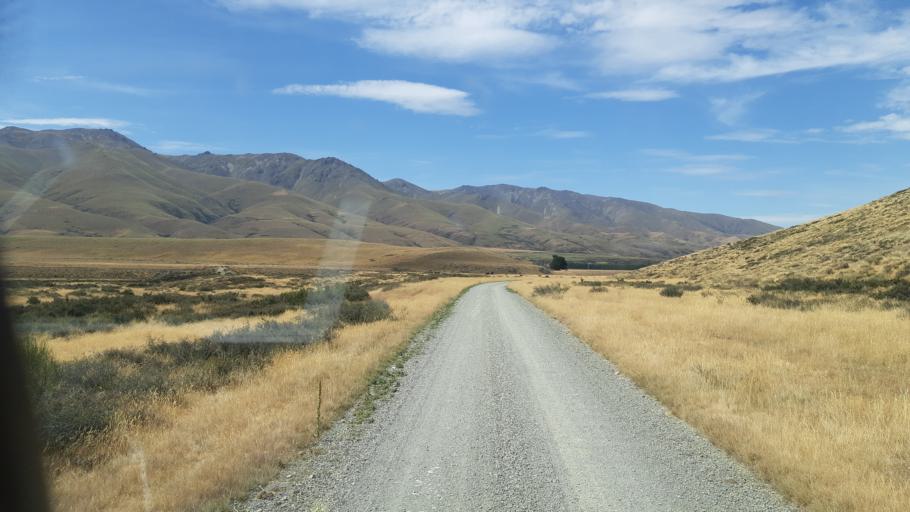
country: NZ
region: Canterbury
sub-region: Timaru District
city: Pleasant Point
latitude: -44.3516
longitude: 170.6295
